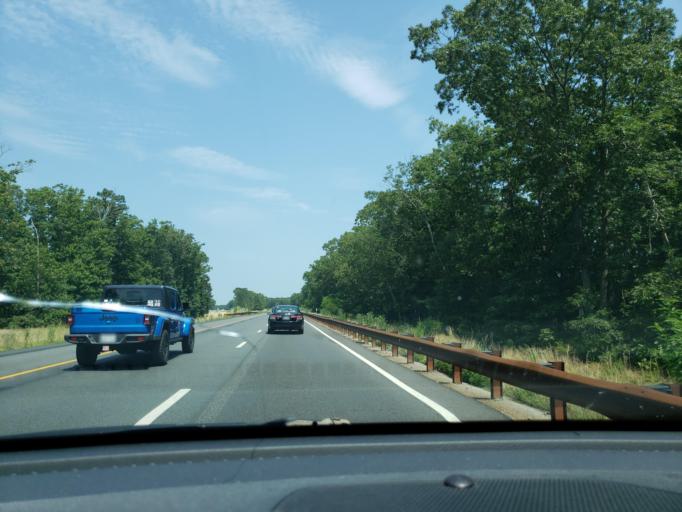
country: US
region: New Jersey
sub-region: Atlantic County
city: Linwood
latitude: 39.3548
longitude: -74.5943
